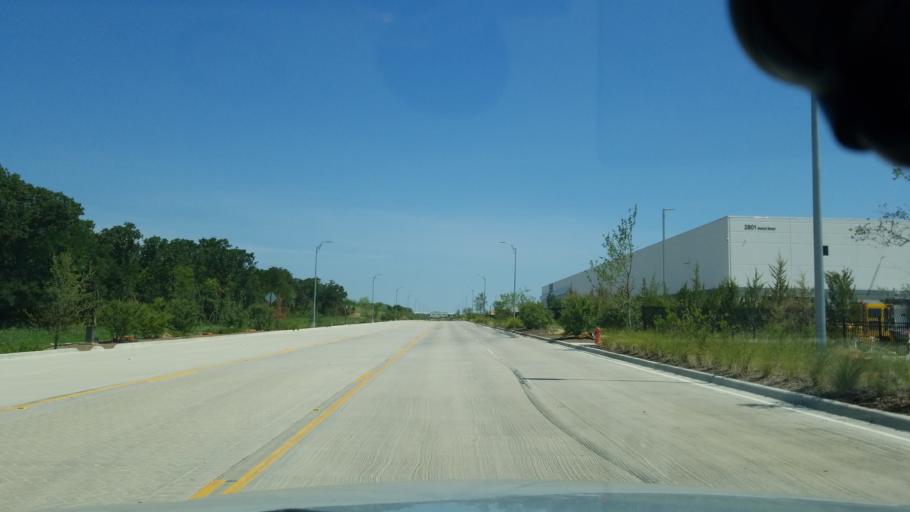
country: US
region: Texas
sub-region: Tarrant County
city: Euless
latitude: 32.8421
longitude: -97.0310
